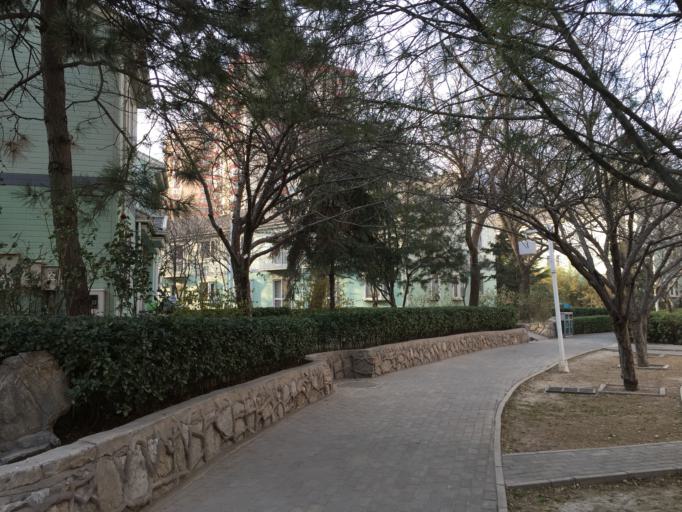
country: CN
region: Beijing
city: Dongfeng
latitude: 39.9466
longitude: 116.4659
